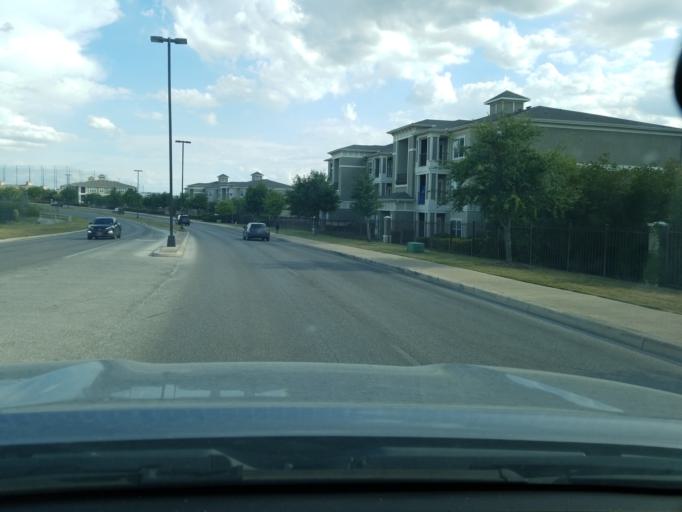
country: US
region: Texas
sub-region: Bexar County
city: Shavano Park
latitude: 29.6011
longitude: -98.5970
